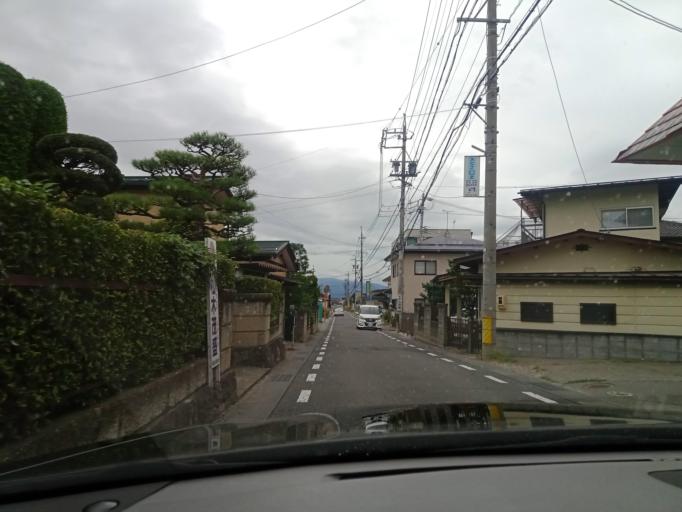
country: JP
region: Nagano
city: Nagano-shi
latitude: 36.6812
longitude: 138.2079
